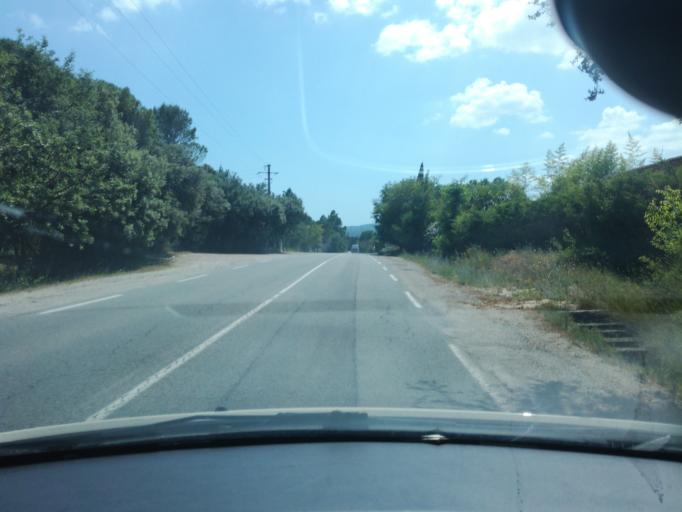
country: FR
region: Provence-Alpes-Cote d'Azur
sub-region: Departement du Var
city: Le Muy
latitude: 43.4855
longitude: 6.5673
